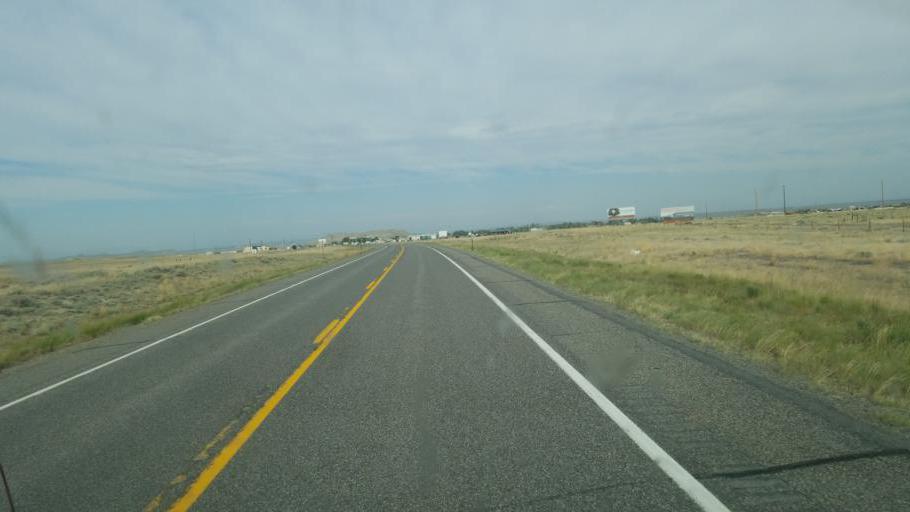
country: US
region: Wyoming
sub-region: Fremont County
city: Riverton
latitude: 43.2369
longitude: -108.0887
